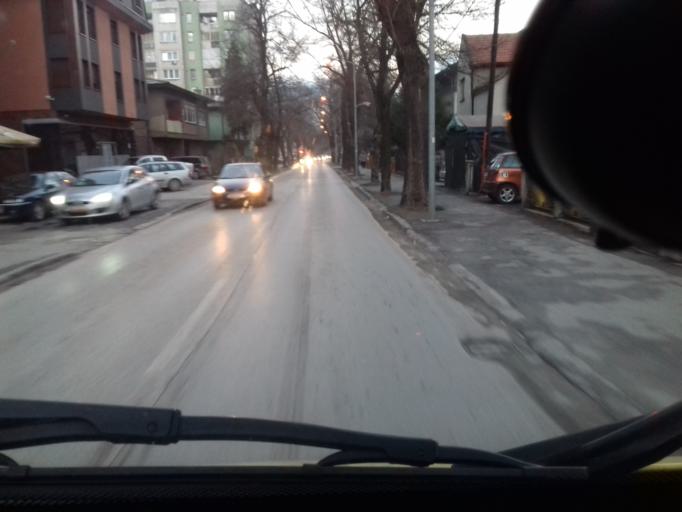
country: BA
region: Federation of Bosnia and Herzegovina
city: Zenica
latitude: 44.1990
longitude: 17.8984
